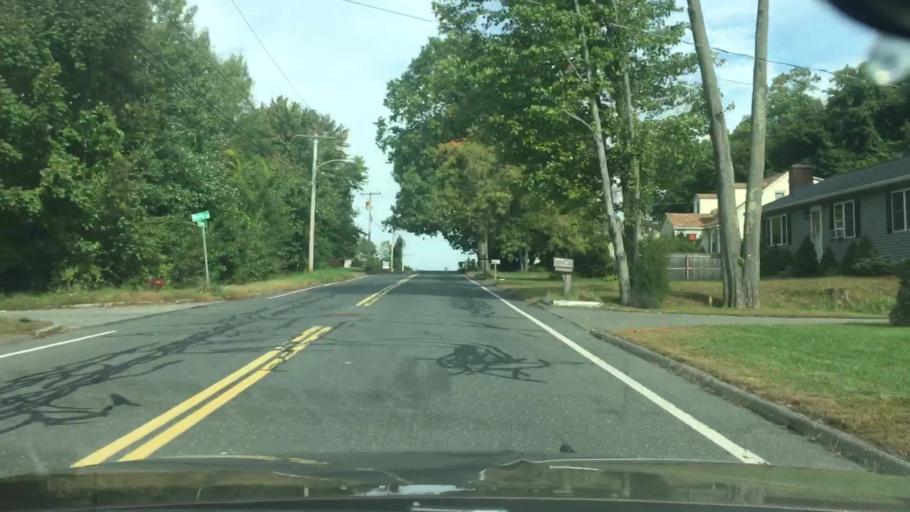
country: US
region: Massachusetts
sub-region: Hampden County
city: East Longmeadow
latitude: 42.0712
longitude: -72.5300
